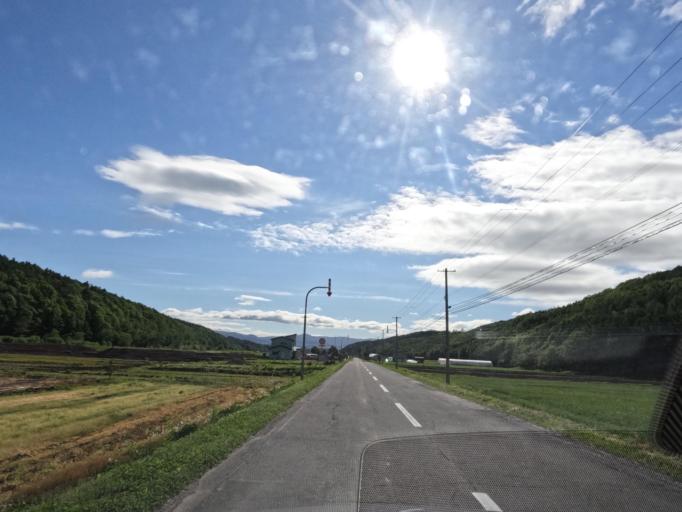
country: JP
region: Hokkaido
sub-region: Asahikawa-shi
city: Asahikawa
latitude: 43.6268
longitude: 142.5179
